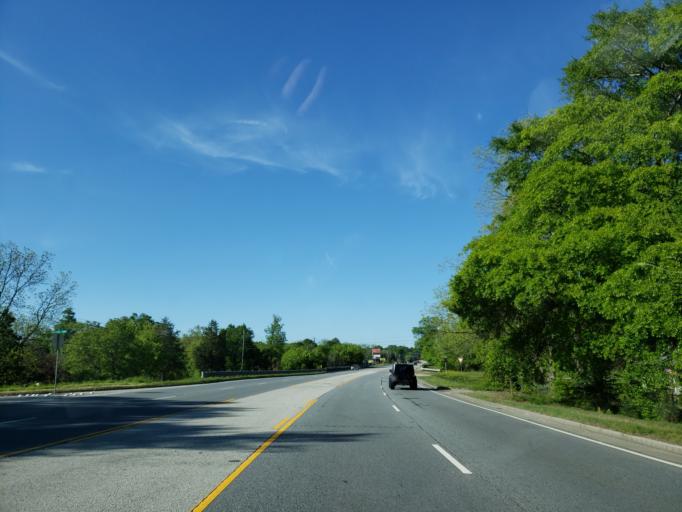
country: US
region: Georgia
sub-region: Polk County
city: Cedartown
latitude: 33.9787
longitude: -85.2577
